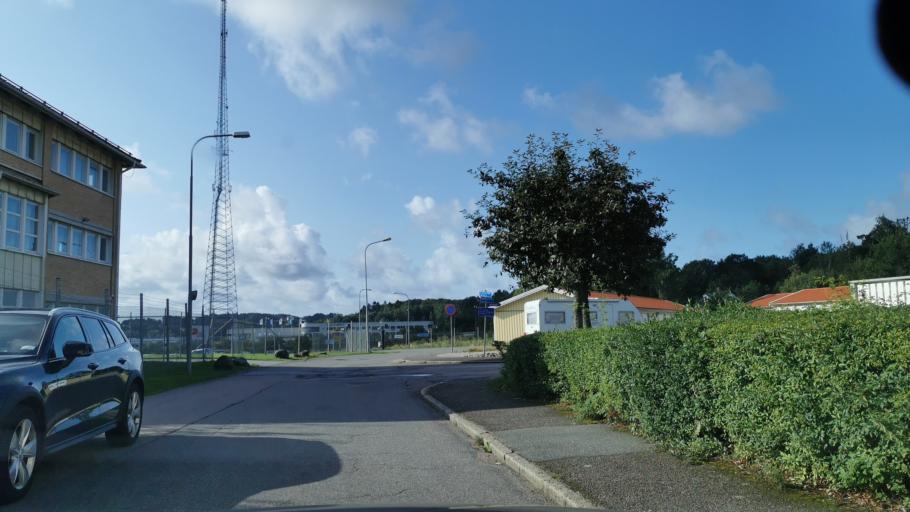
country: SE
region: Vaestra Goetaland
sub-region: Goteborg
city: Majorna
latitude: 57.6491
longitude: 11.9257
